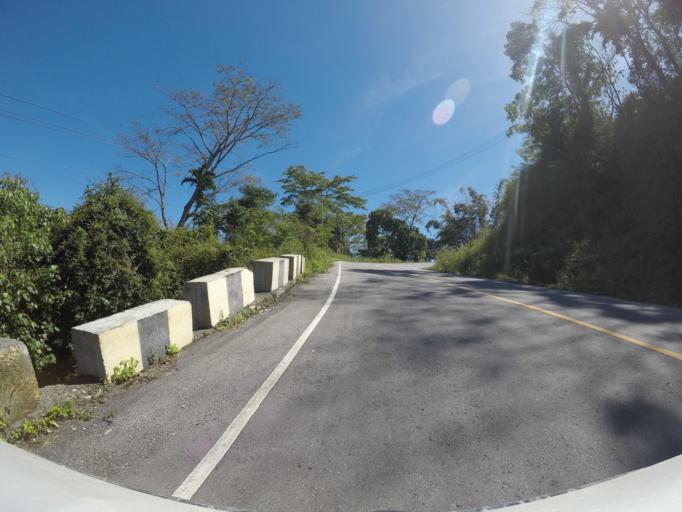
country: TL
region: Manufahi
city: Same
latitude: -8.9010
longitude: 125.9771
